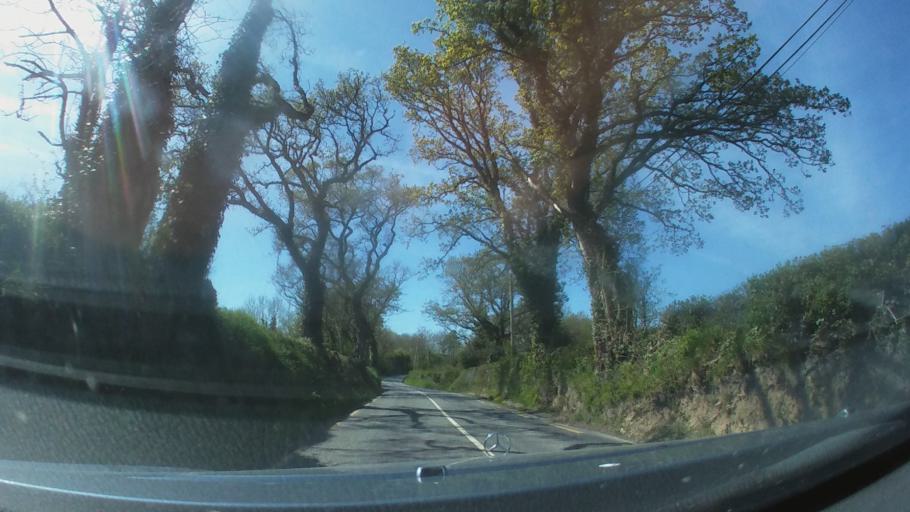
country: IE
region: Leinster
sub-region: Kilkenny
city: Kilkenny
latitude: 52.6423
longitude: -7.3035
